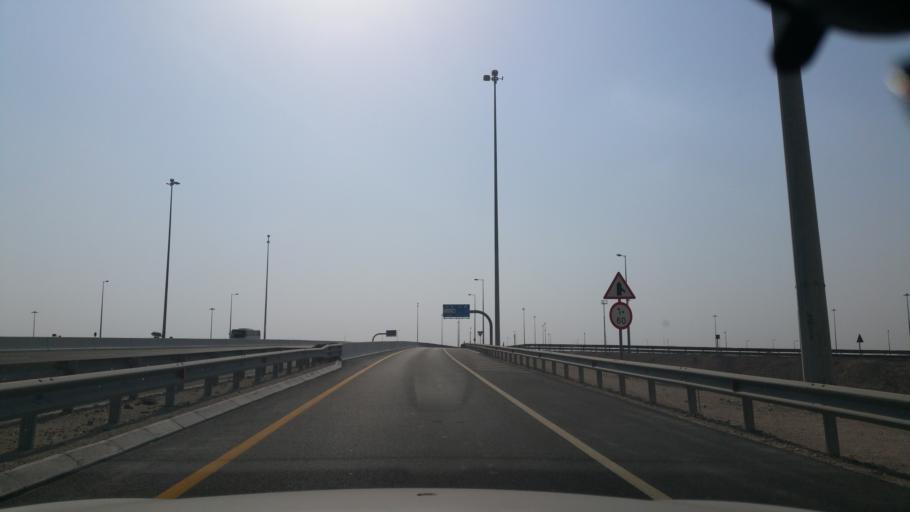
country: QA
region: Baladiyat Umm Salal
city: Umm Salal `Ali
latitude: 25.4494
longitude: 51.4134
